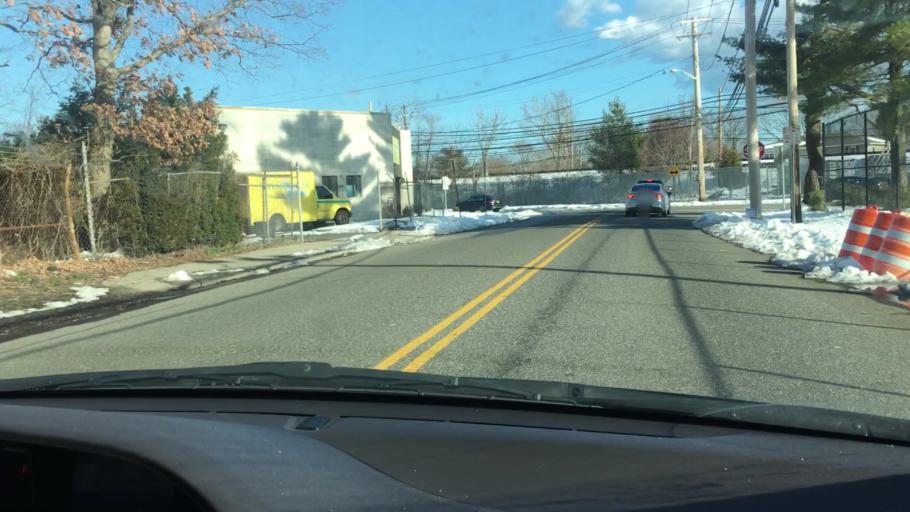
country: US
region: New York
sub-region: Suffolk County
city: Deer Park
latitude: 40.7609
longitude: -73.3343
